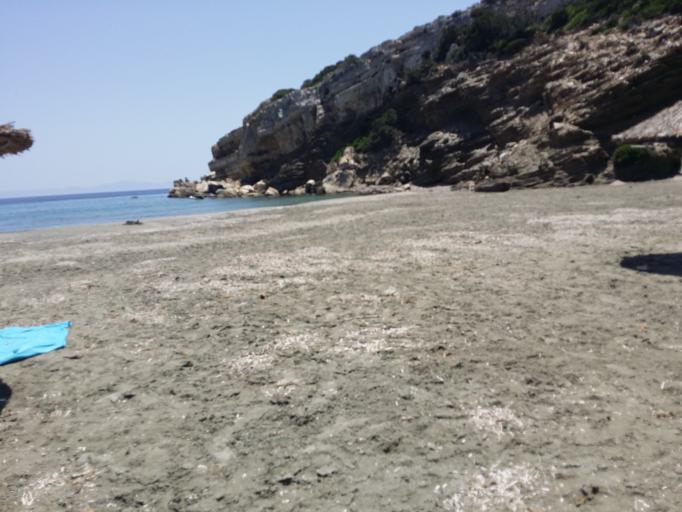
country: GR
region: South Aegean
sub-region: Nomos Kykladon
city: Antiparos
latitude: 36.9553
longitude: 24.9994
